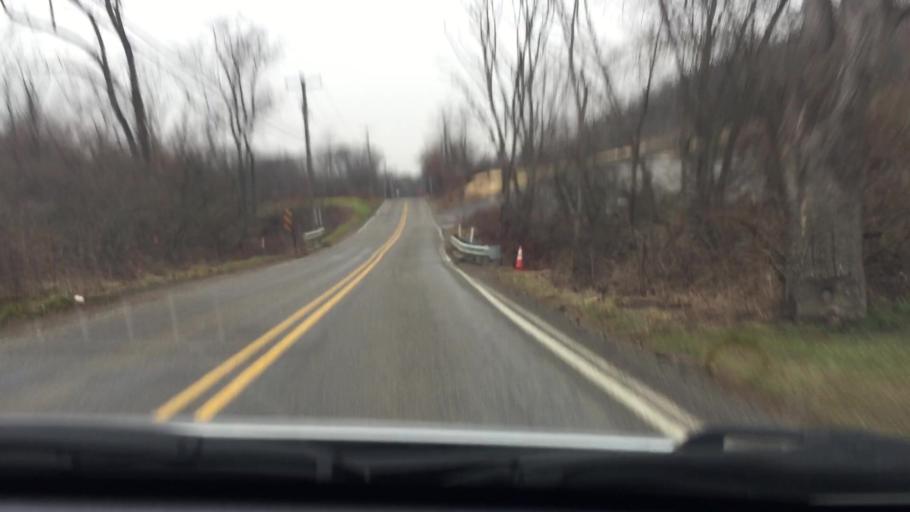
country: US
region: Pennsylvania
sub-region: Beaver County
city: Conway
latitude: 40.6806
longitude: -80.2042
